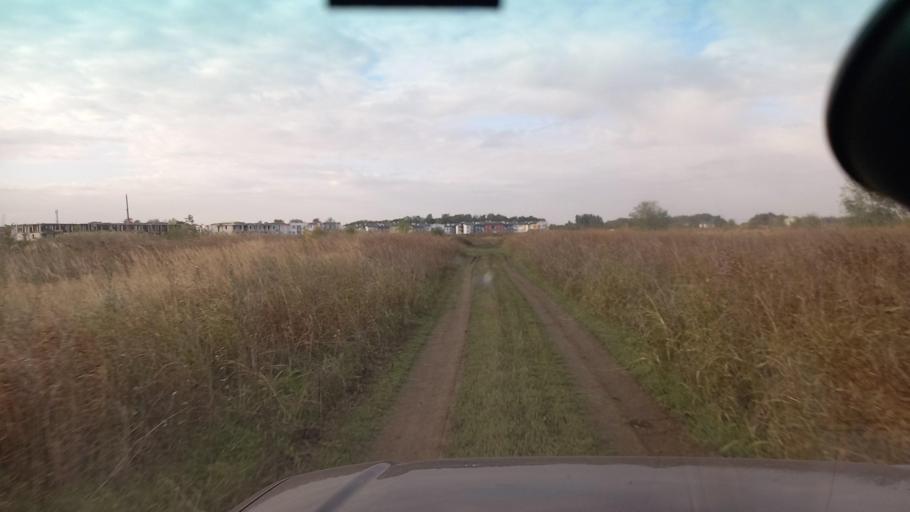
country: RU
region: Krasnodarskiy
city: Krasnodar
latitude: 45.1286
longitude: 38.9129
